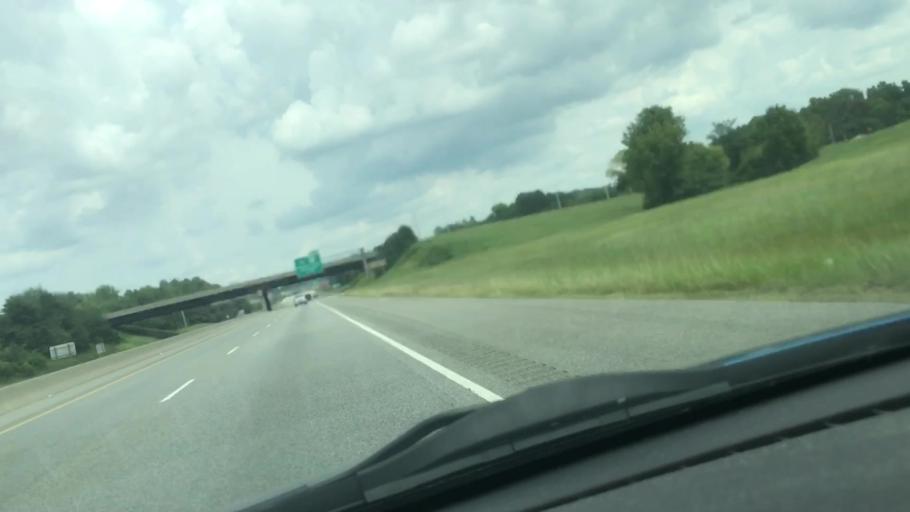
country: US
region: North Carolina
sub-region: Guilford County
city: Greensboro
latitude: 36.0261
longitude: -79.8246
